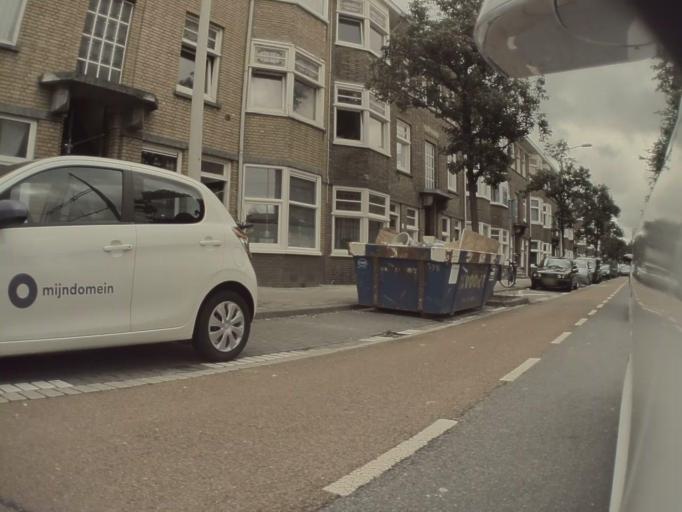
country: NL
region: South Holland
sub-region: Gemeente Den Haag
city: The Hague
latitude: 52.0558
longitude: 4.2999
